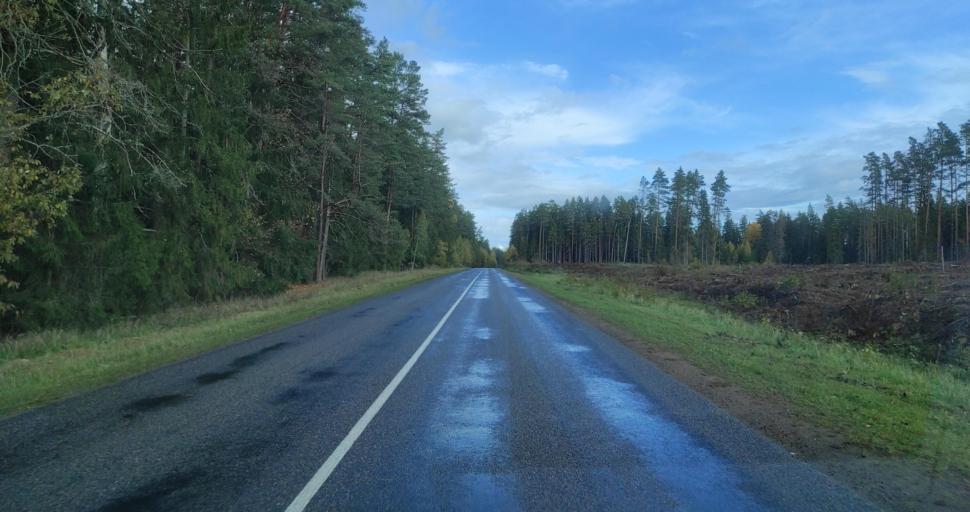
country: LV
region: Skrunda
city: Skrunda
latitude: 56.6372
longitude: 22.0063
